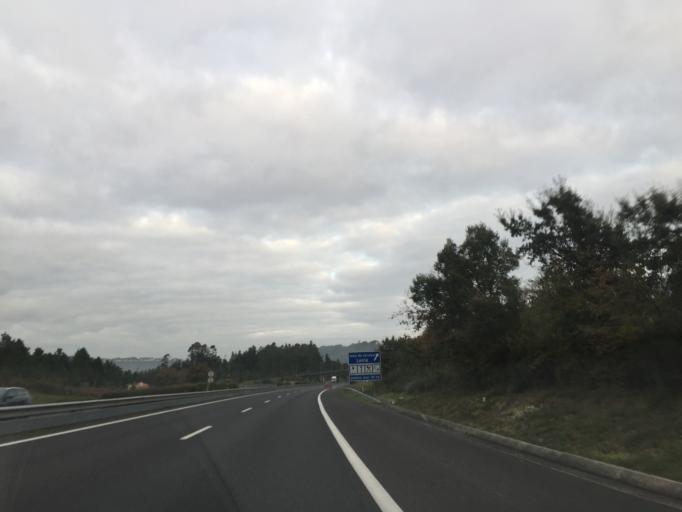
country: PT
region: Leiria
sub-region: Leiria
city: Santa Catarina da Serra
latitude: 39.7062
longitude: -8.7061
